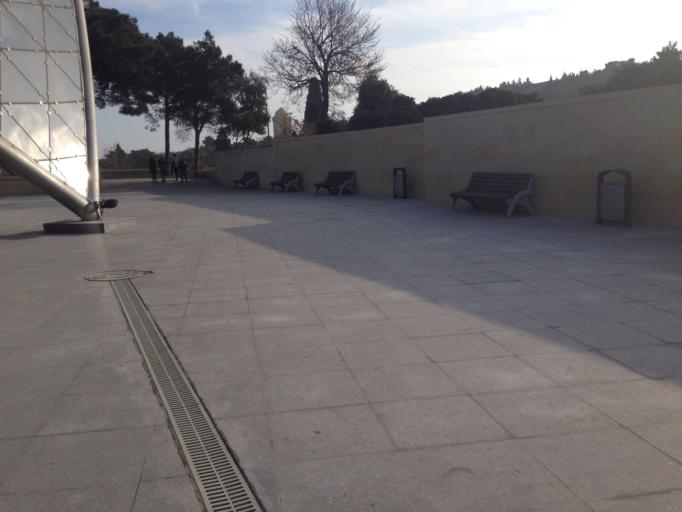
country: AZ
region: Baki
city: Badamdar
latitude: 40.3585
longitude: 49.8283
